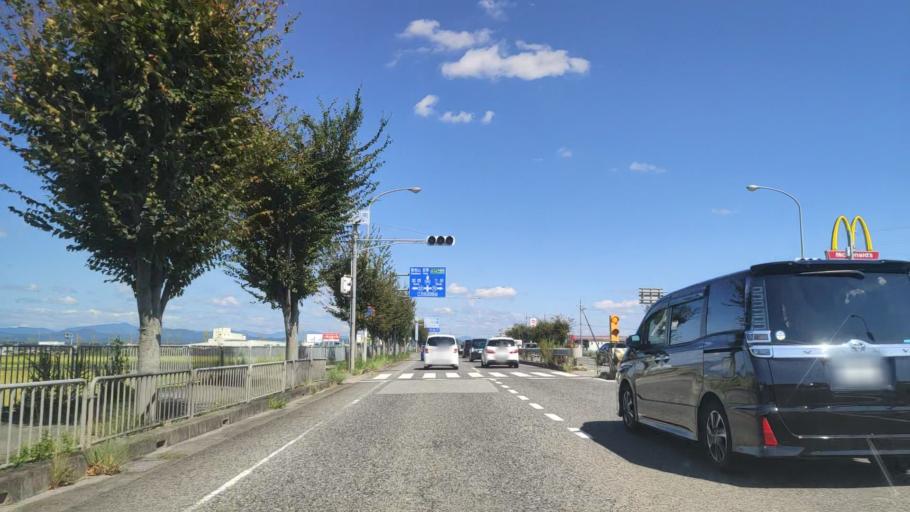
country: JP
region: Hyogo
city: Ono
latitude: 34.8552
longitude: 134.9498
